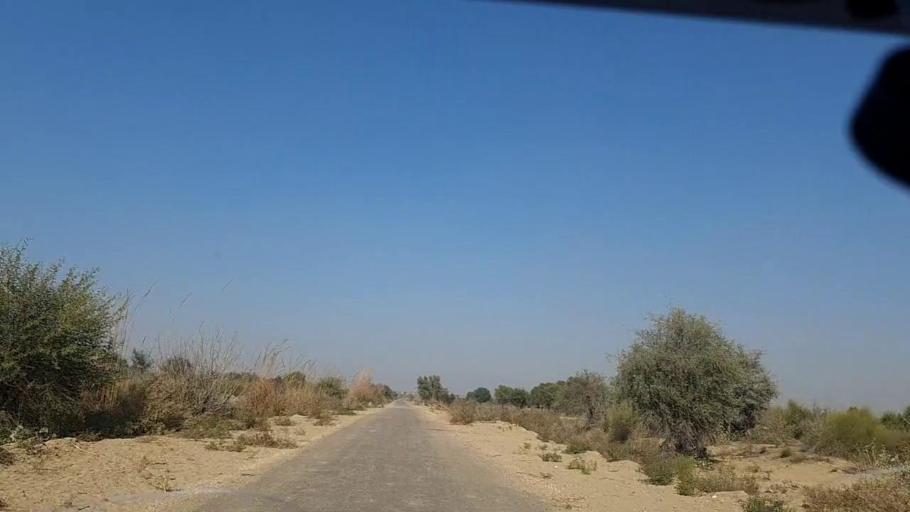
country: PK
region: Sindh
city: Khanpur
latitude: 27.5687
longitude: 69.3797
